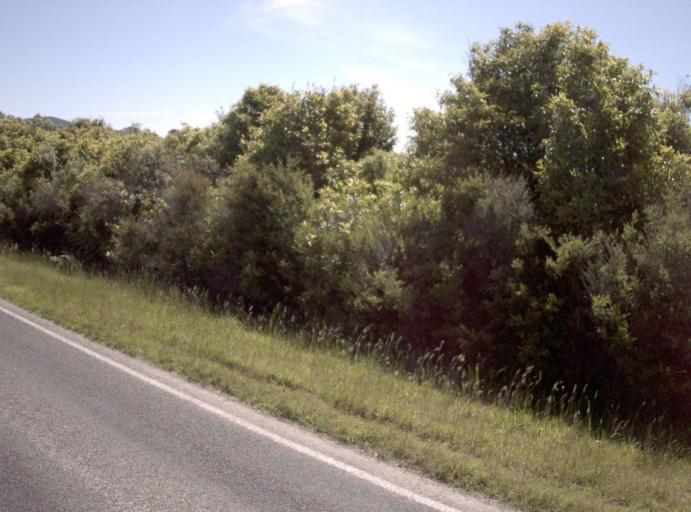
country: AU
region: Victoria
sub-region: Latrobe
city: Morwell
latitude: -38.6845
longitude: 146.1896
